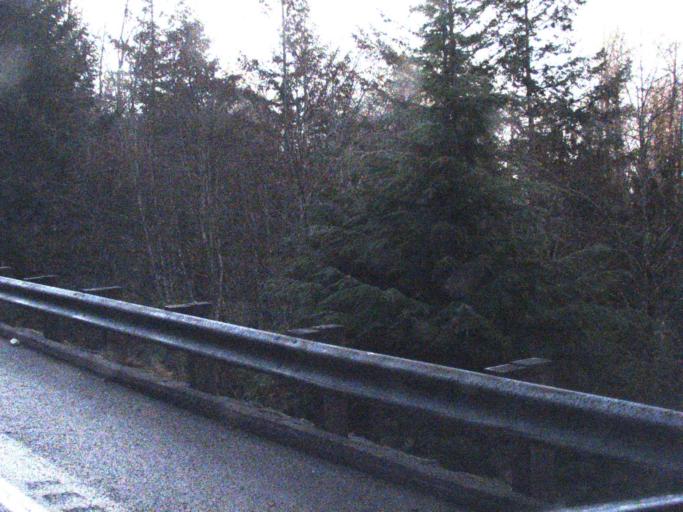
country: US
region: Washington
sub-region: Snohomish County
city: Darrington
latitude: 48.5016
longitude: -121.6486
